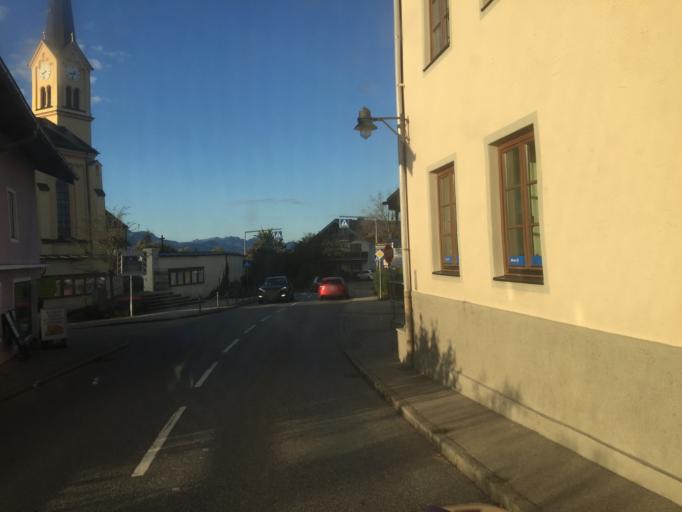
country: DE
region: Bavaria
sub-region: Upper Bavaria
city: Chieming
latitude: 47.8930
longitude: 12.5414
